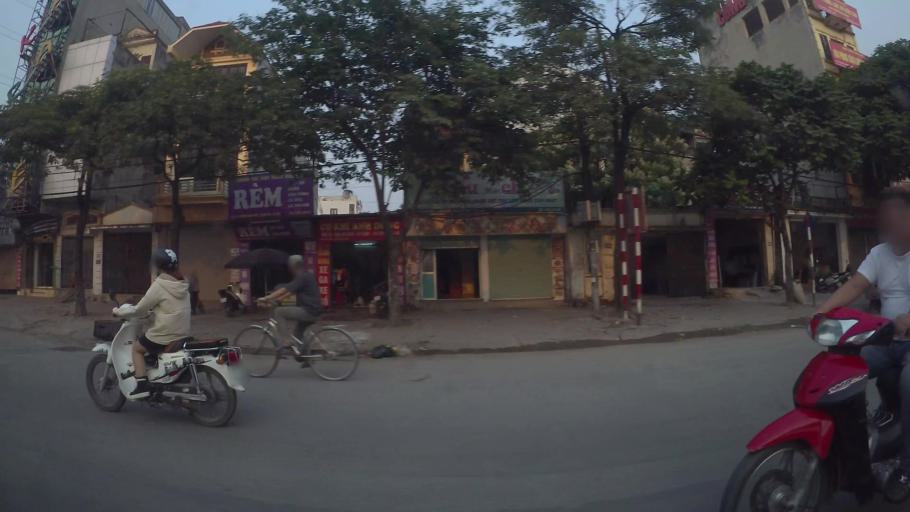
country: VN
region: Ha Noi
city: Van Dien
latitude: 20.9421
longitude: 105.8441
